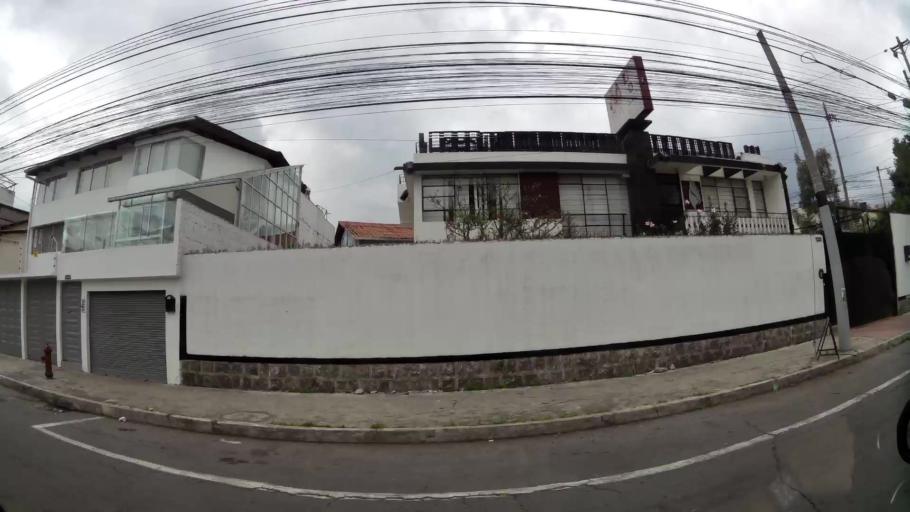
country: EC
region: Pichincha
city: Quito
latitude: -0.1678
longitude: -78.4785
